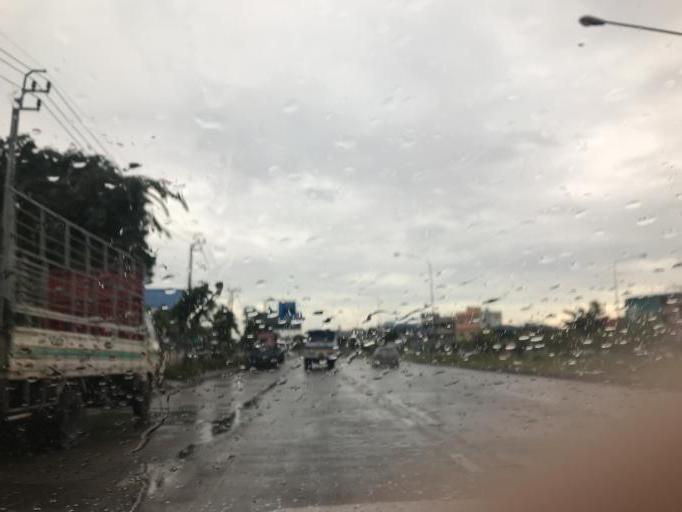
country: TH
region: Bangkok
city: Bangkok Noi
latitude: 13.7545
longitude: 100.4659
